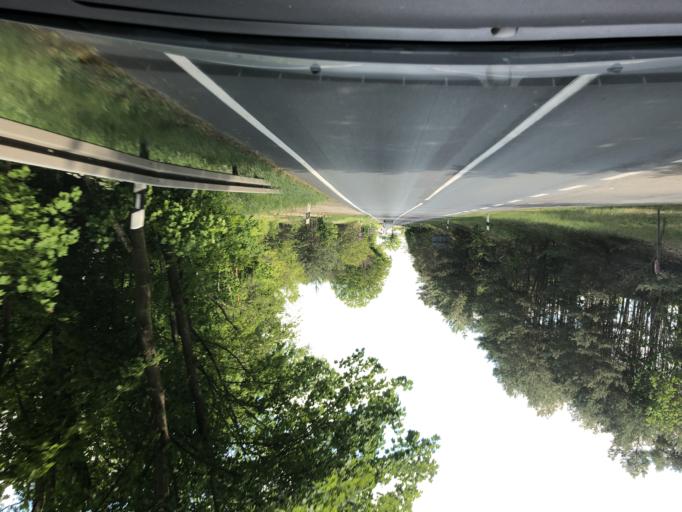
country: DE
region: Brandenburg
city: Spreenhagen
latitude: 52.3219
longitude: 13.9023
